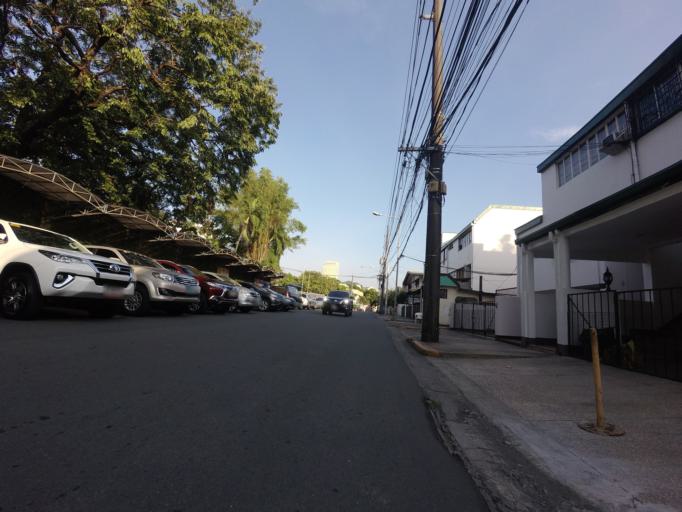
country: PH
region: Metro Manila
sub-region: San Juan
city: San Juan
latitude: 14.6035
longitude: 121.0397
